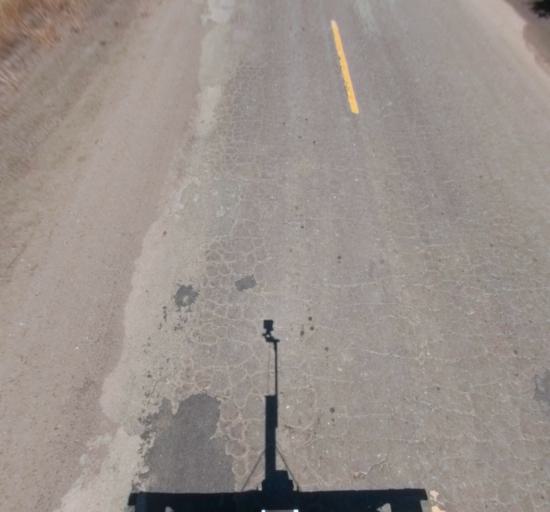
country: US
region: California
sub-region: Madera County
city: Chowchilla
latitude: 37.0442
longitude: -120.2745
